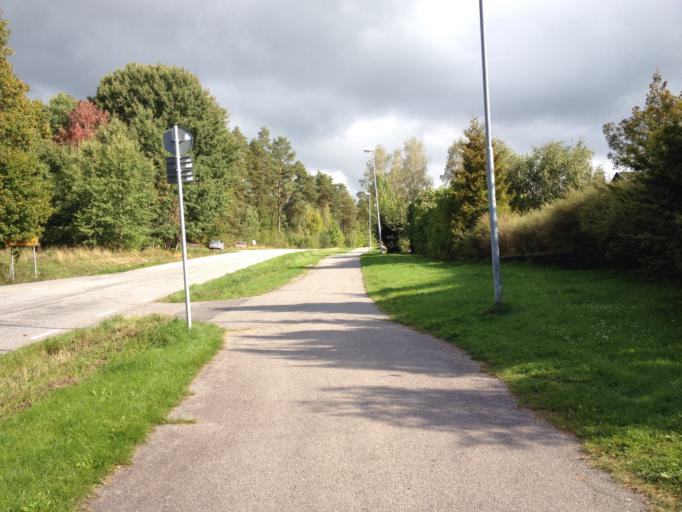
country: SE
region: OEstergoetland
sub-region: Linkopings Kommun
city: Sturefors
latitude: 58.3048
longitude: 15.8679
